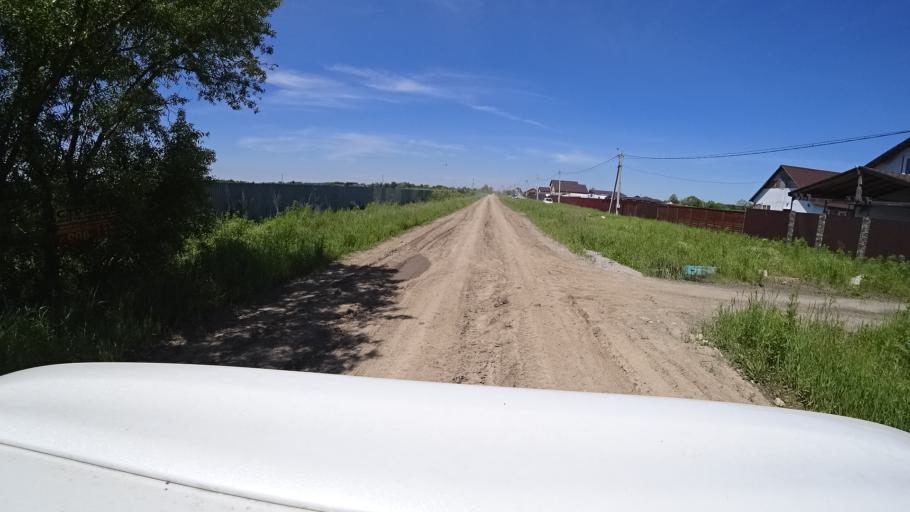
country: RU
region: Khabarovsk Krai
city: Topolevo
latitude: 48.5095
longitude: 135.2038
